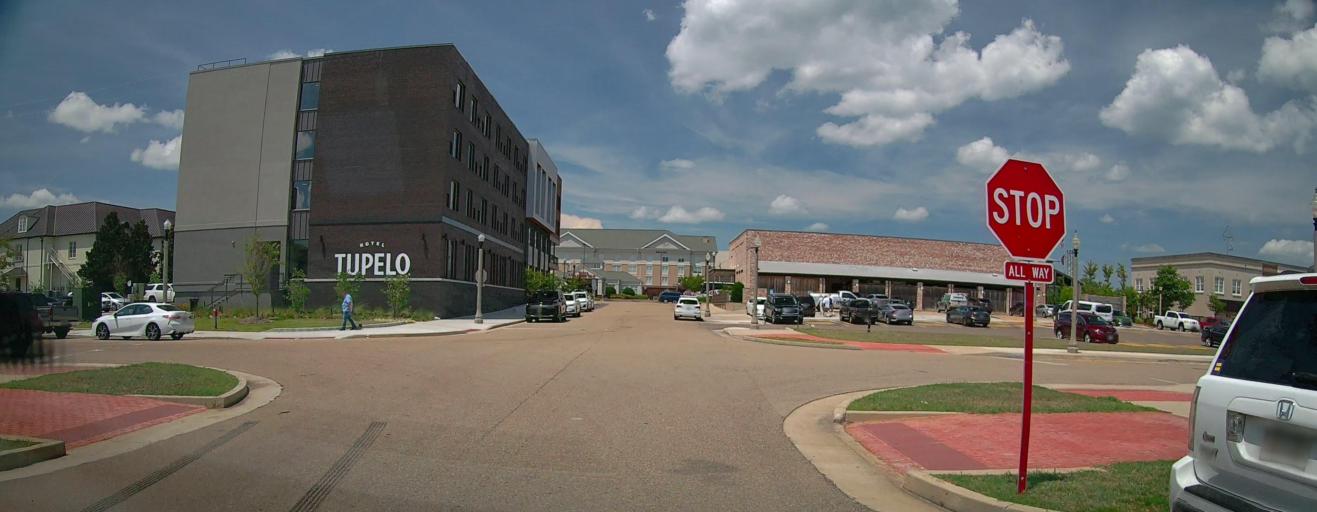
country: US
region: Mississippi
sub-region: Lee County
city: Tupelo
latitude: 34.2564
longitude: -88.6996
